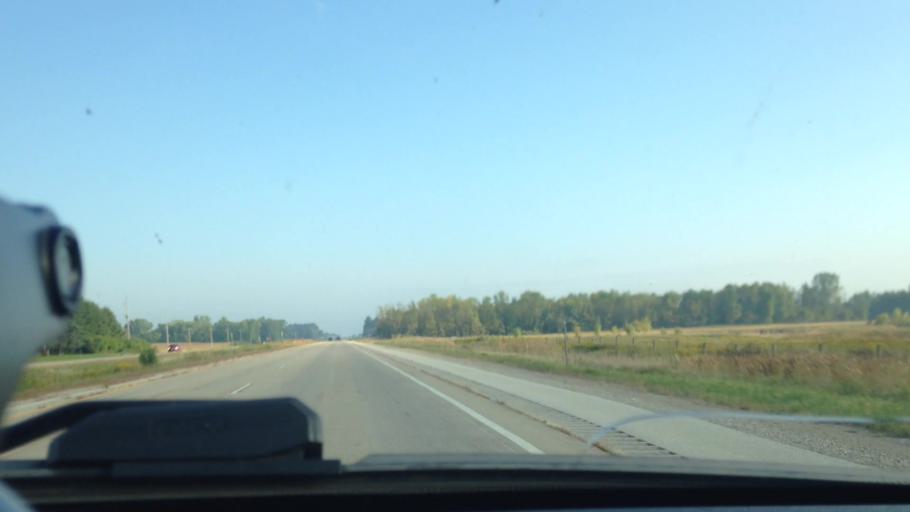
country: US
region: Wisconsin
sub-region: Oconto County
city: Oconto Falls
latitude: 45.0137
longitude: -88.0455
